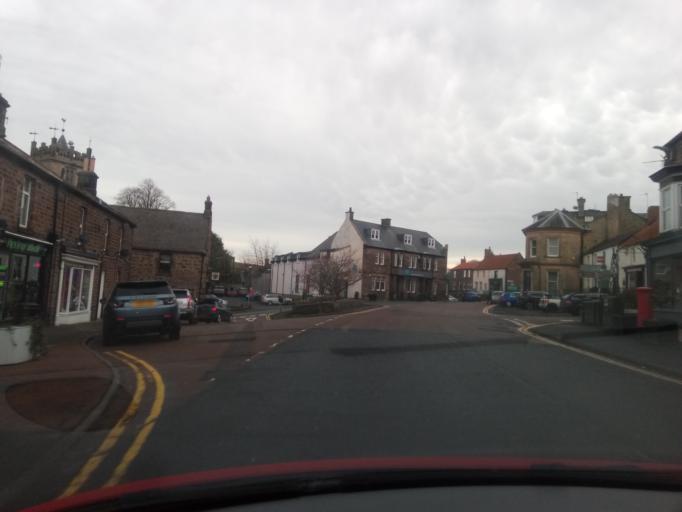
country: GB
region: England
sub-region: Northumberland
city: Wooler
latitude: 55.5460
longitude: -2.0150
